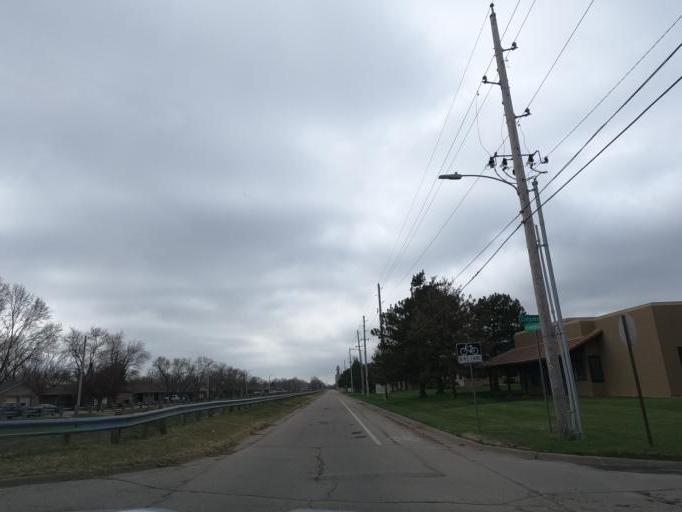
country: US
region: Kansas
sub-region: Reno County
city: Hutchinson
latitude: 38.0846
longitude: -97.9131
